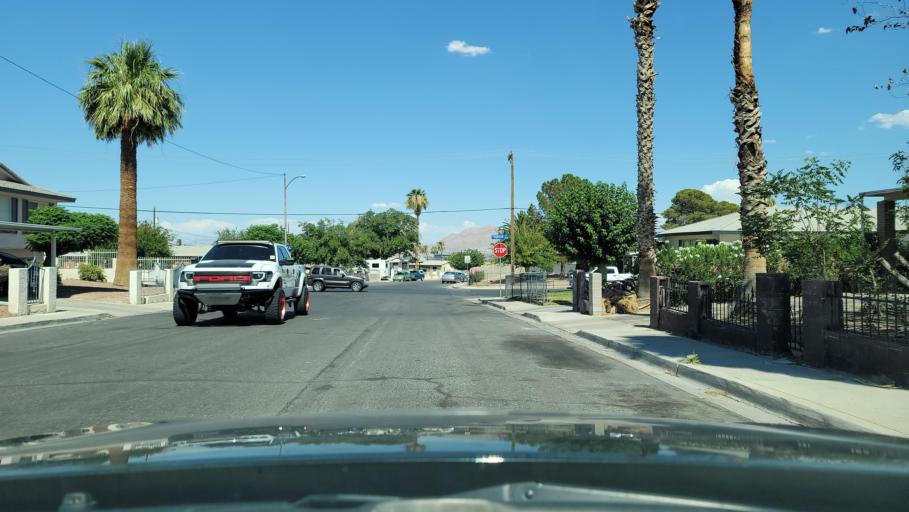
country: US
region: Nevada
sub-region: Clark County
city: Las Vegas
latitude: 36.2013
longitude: -115.1480
